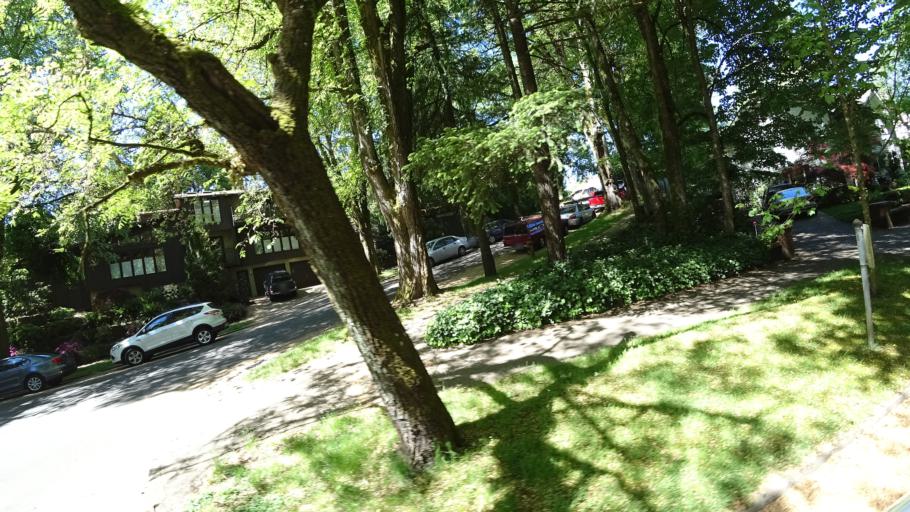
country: US
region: Oregon
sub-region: Multnomah County
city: Portland
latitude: 45.5224
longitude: -122.6255
